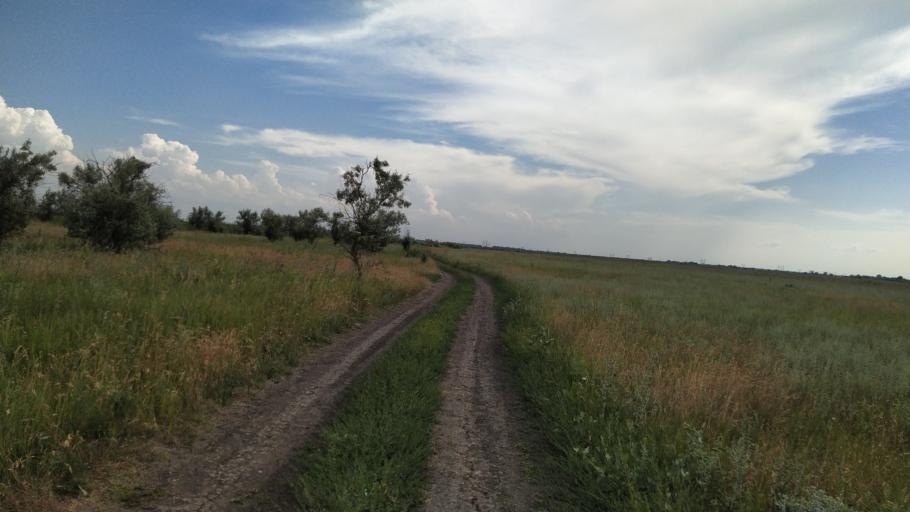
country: RU
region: Rostov
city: Kuleshovka
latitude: 47.1368
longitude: 39.6333
